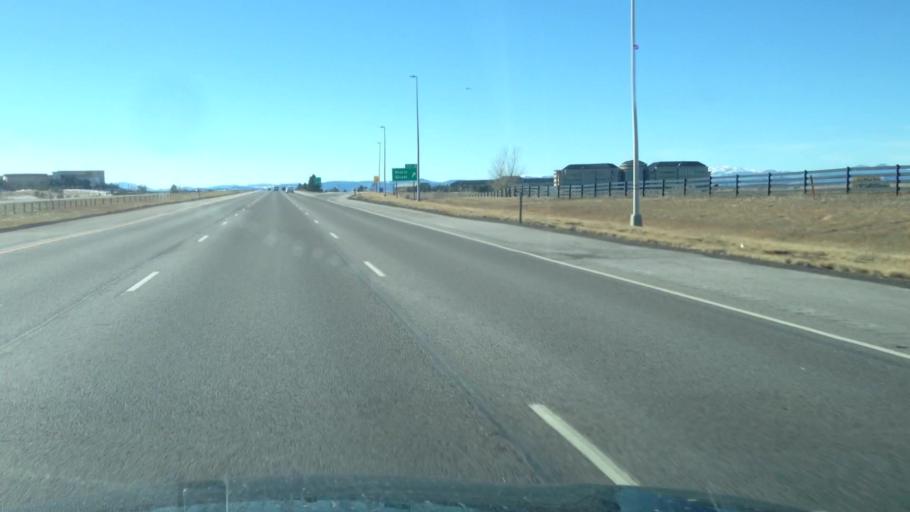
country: US
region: Colorado
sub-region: Arapahoe County
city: Dove Valley
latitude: 39.5542
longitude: -104.8327
